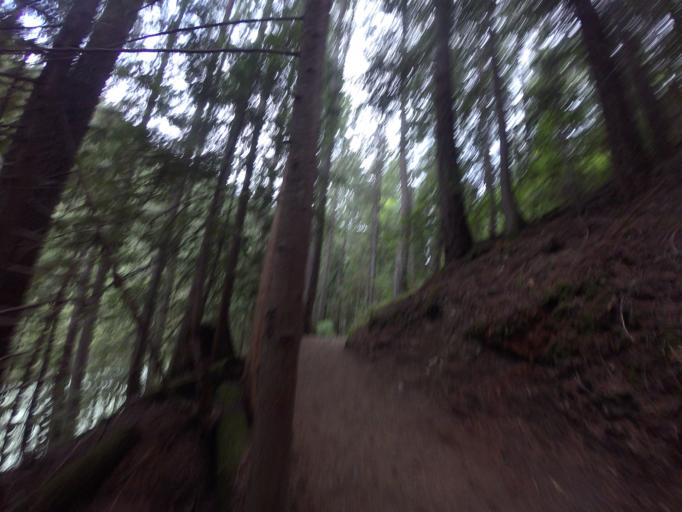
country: CA
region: British Columbia
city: Pemberton
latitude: 50.2921
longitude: -122.8300
